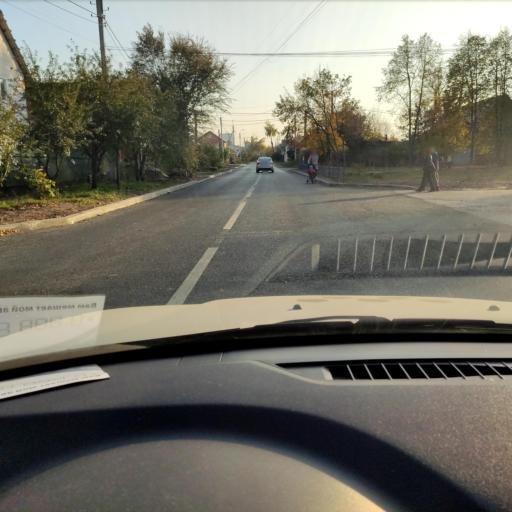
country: RU
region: Samara
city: Tol'yatti
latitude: 53.5304
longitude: 49.4187
